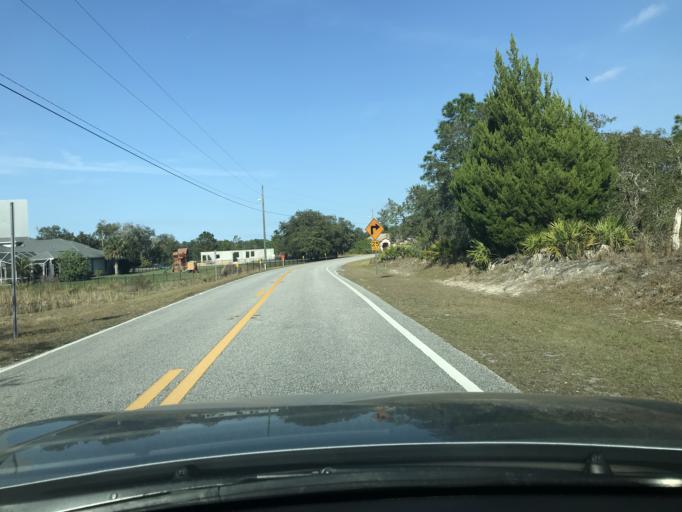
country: US
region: Florida
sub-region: Hernando County
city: North Weeki Wachee
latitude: 28.5525
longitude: -82.5528
